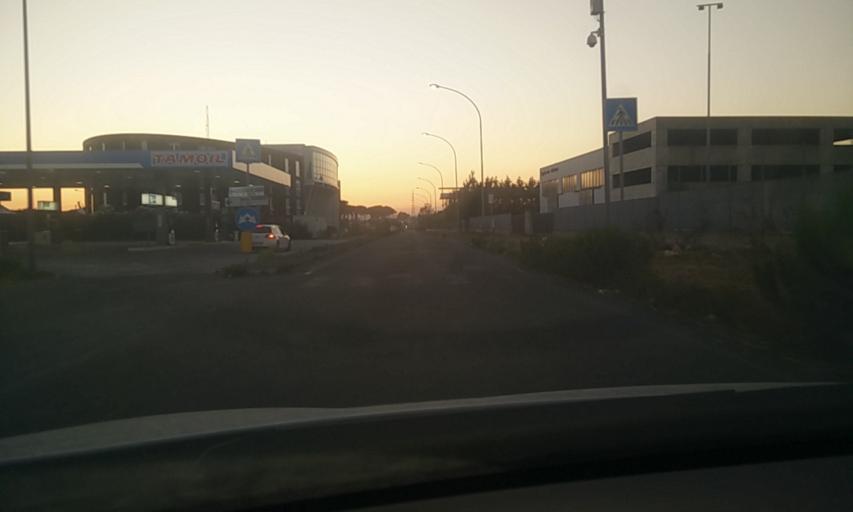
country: IT
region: Tuscany
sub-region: Provincia di Massa-Carrara
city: Massa
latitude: 44.0302
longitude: 10.0917
